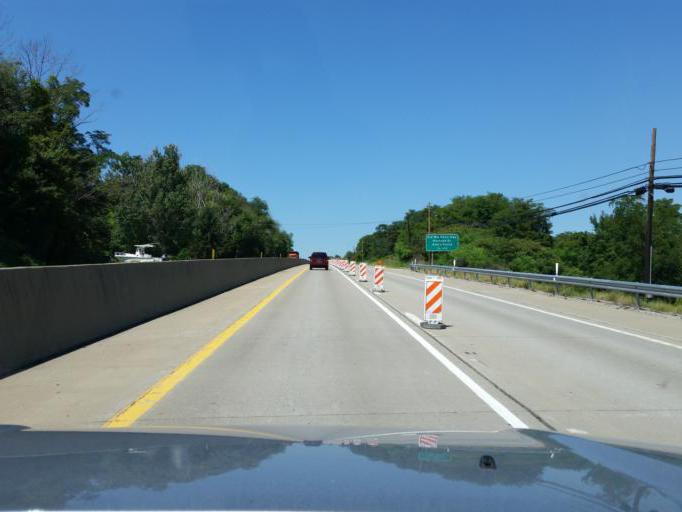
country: US
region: Pennsylvania
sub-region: Westmoreland County
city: Latrobe
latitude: 40.3972
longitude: -79.4572
